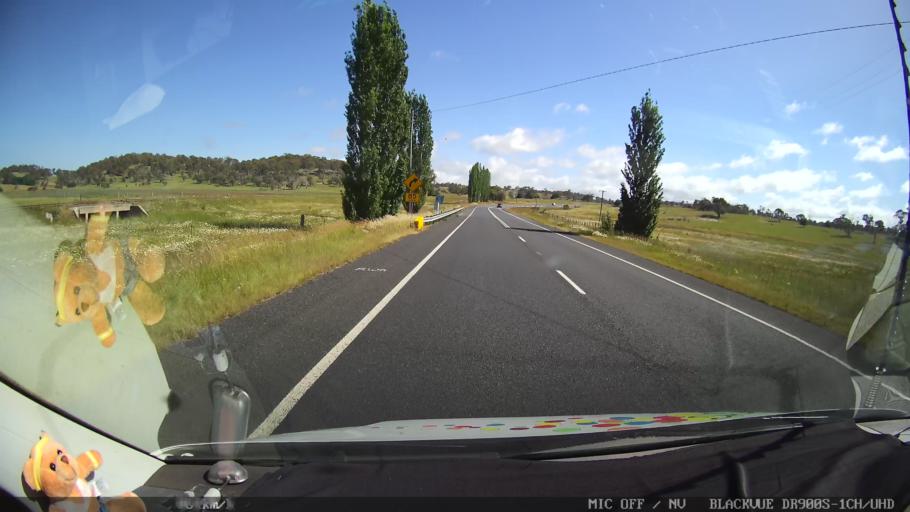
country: AU
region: New South Wales
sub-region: Guyra
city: Guyra
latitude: -30.1256
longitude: 151.6852
